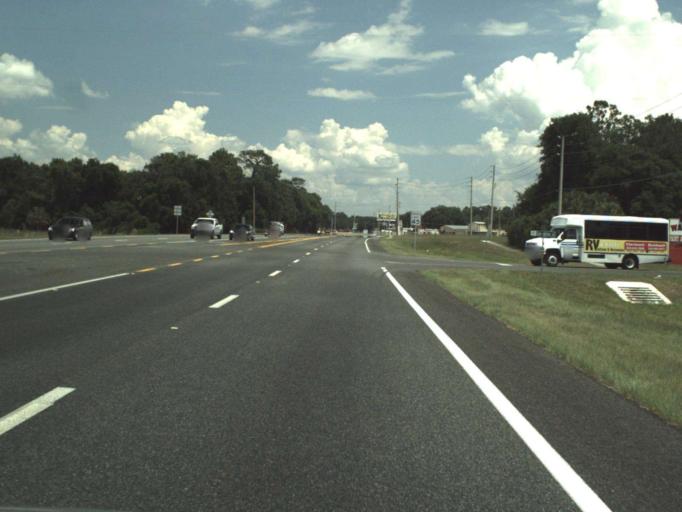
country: US
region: Florida
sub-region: Lake County
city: Leesburg
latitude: 28.8131
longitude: -81.9309
